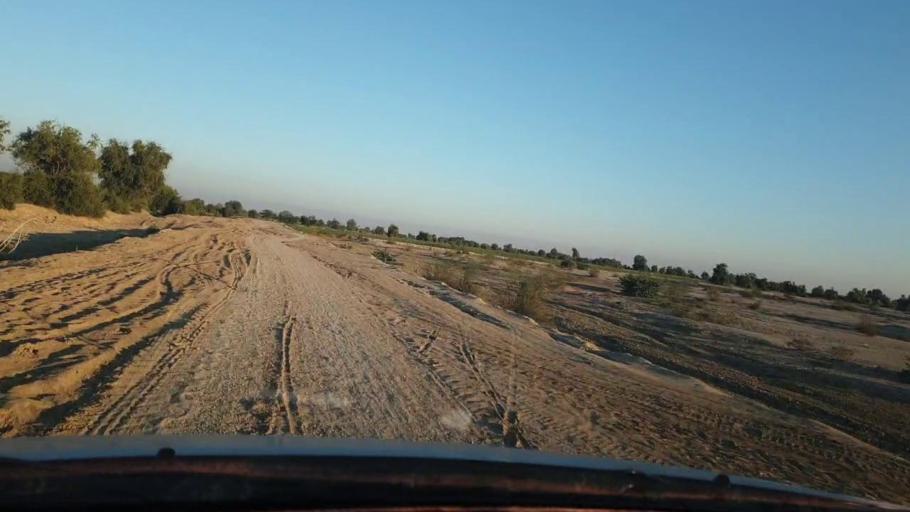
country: PK
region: Sindh
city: Johi
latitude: 26.8068
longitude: 67.4784
